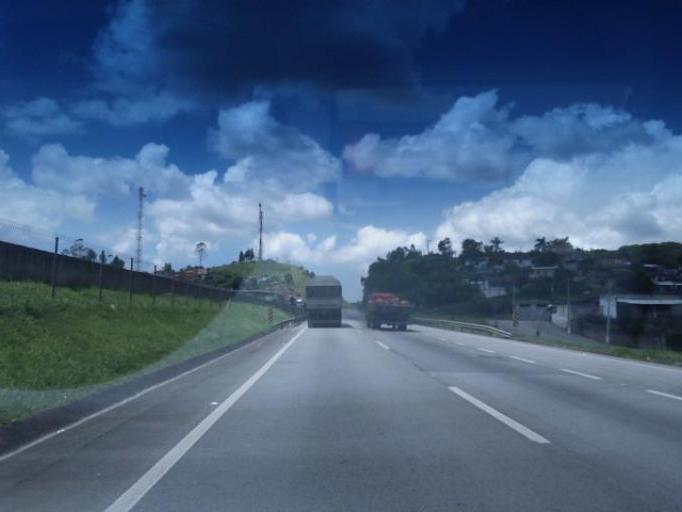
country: BR
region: Sao Paulo
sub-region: Juquitiba
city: Juquitiba
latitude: -23.9814
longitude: -47.1457
